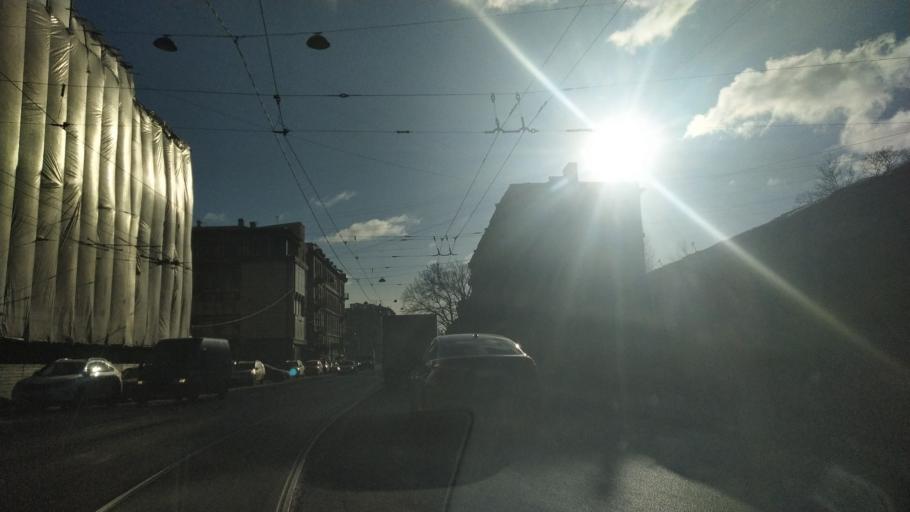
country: RU
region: Leningrad
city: Finlyandskiy
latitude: 59.9599
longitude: 30.3540
